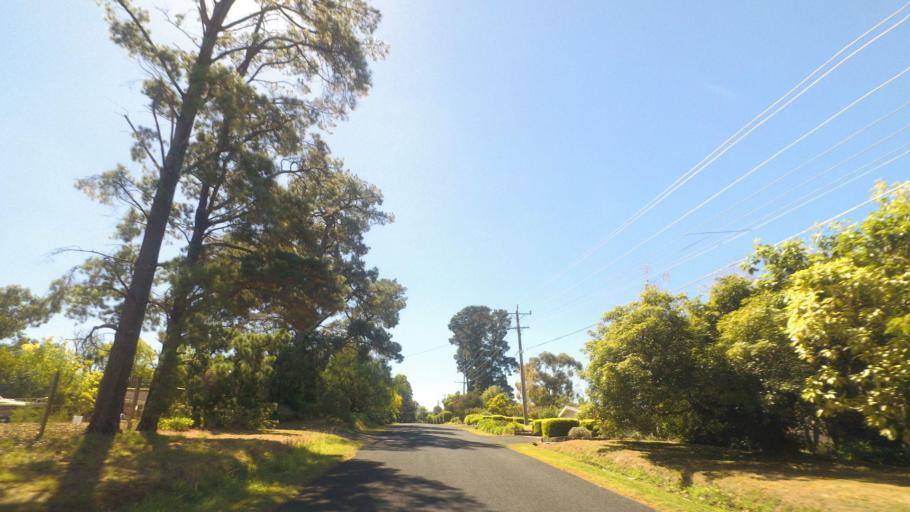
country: AU
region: Victoria
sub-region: Manningham
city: Donvale
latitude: -37.7923
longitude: 145.1866
